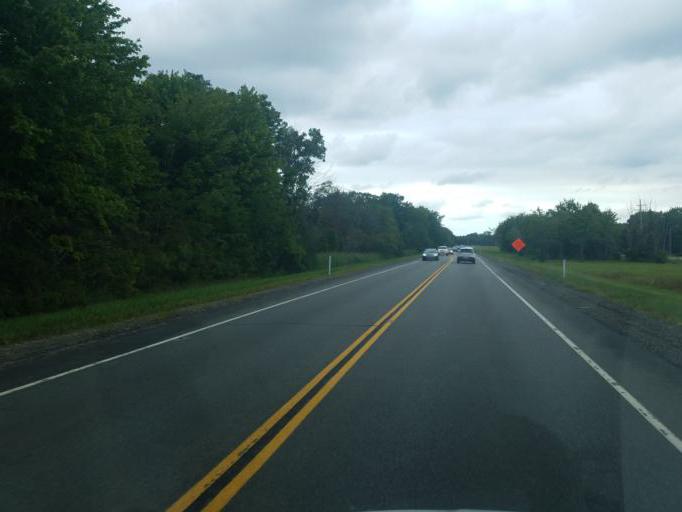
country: US
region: Ohio
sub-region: Lake County
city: Painesville
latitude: 41.6494
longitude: -81.2413
